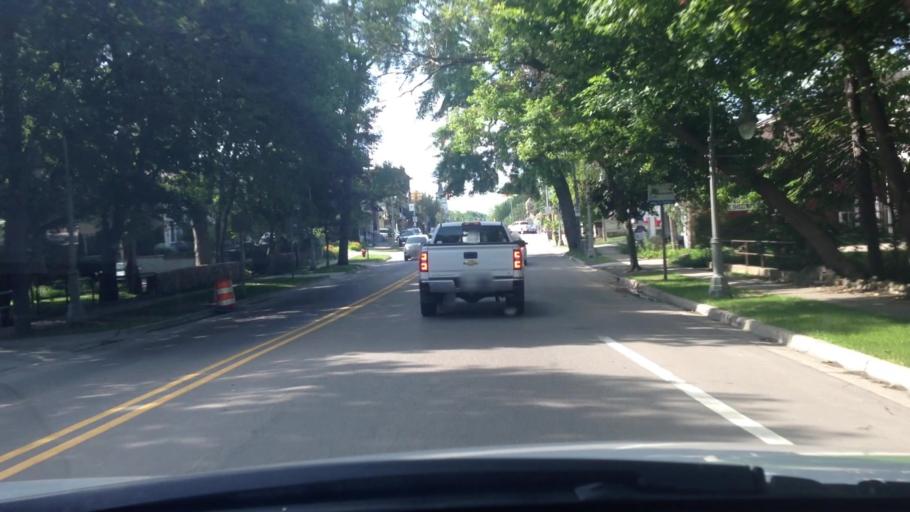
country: US
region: Michigan
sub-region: Oakland County
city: Clarkston
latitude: 42.7371
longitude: -83.4192
